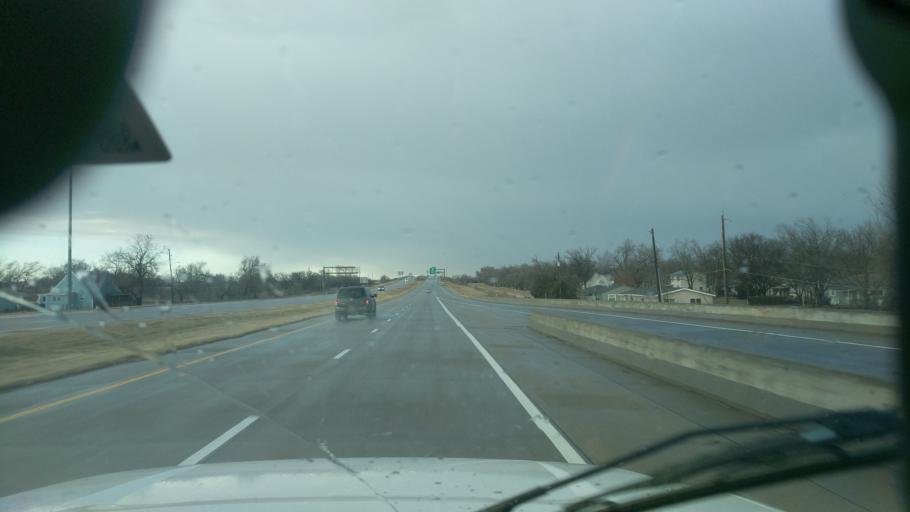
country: US
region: Kansas
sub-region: Harvey County
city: Newton
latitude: 38.0523
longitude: -97.3224
